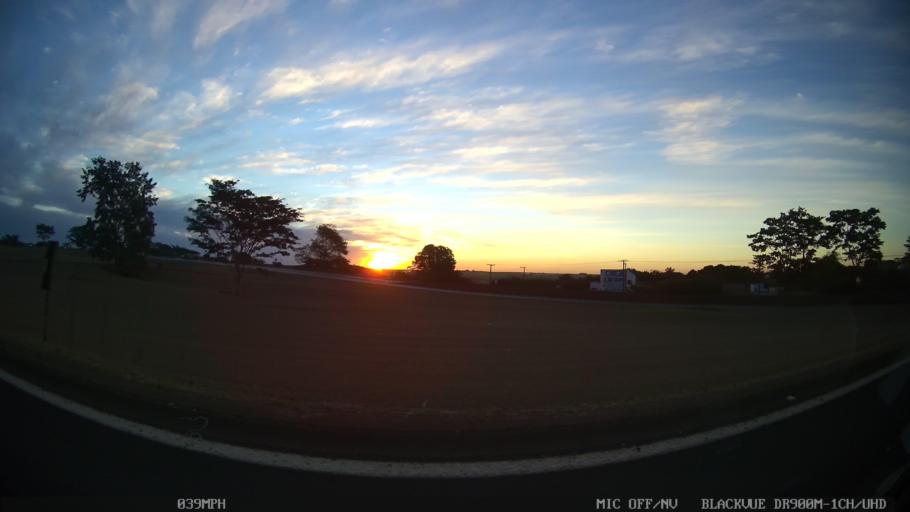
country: BR
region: Sao Paulo
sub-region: Catanduva
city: Catanduva
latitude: -21.1330
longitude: -49.0181
